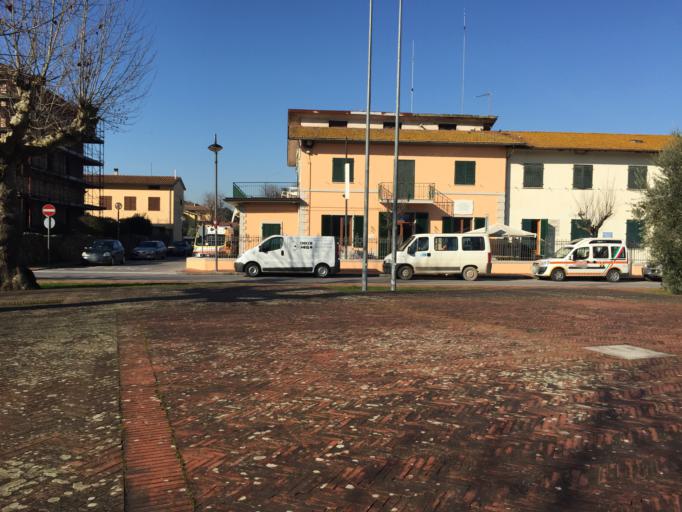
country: IT
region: Tuscany
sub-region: Provincia di Pistoia
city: Ponte Buggianese
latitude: 43.8426
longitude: 10.7477
